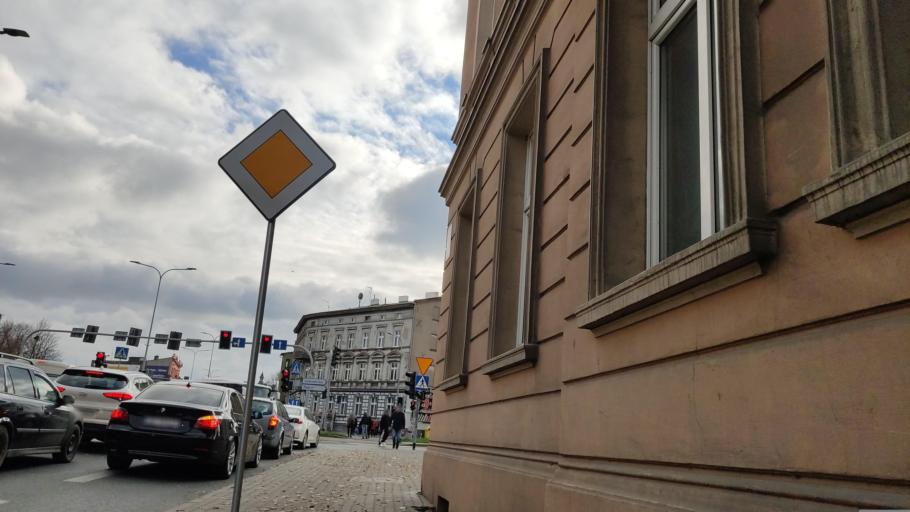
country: PL
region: Kujawsko-Pomorskie
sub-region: Powiat inowroclawski
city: Inowroclaw
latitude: 52.8022
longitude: 18.2512
